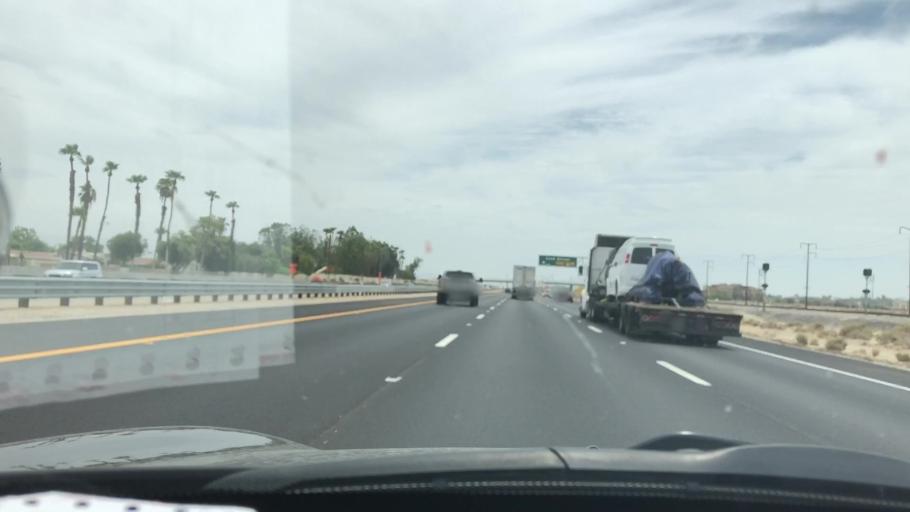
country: US
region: California
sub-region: Riverside County
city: Thousand Palms
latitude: 33.7910
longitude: -116.3633
